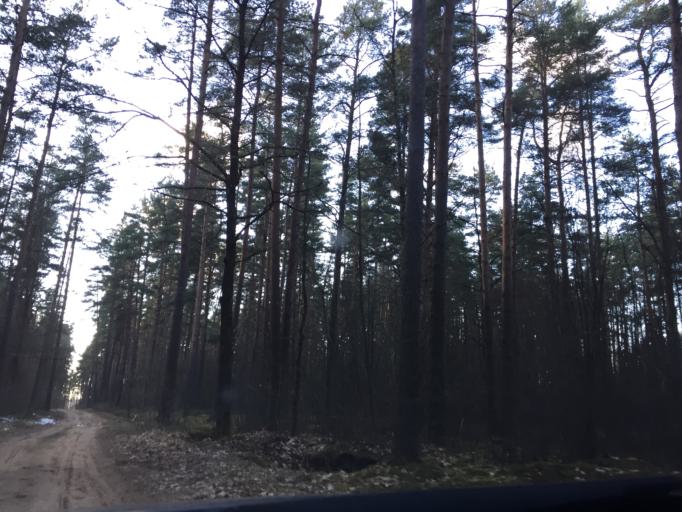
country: LV
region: Kekava
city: Kekava
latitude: 56.8647
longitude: 24.2050
